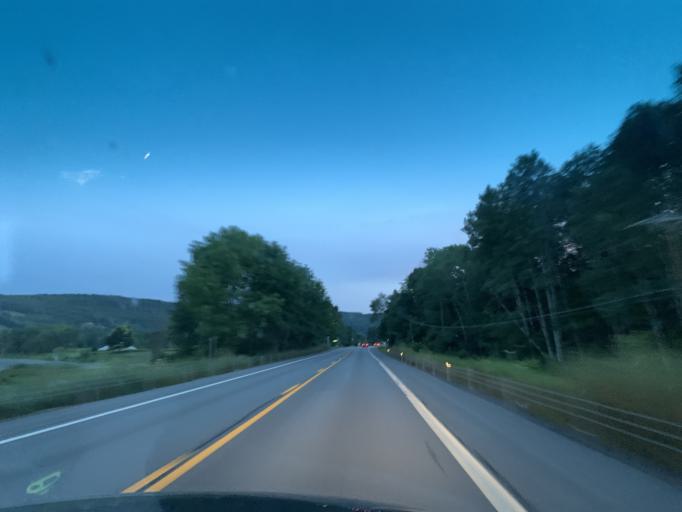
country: US
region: New York
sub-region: Chenango County
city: New Berlin
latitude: 42.5749
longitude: -75.3388
